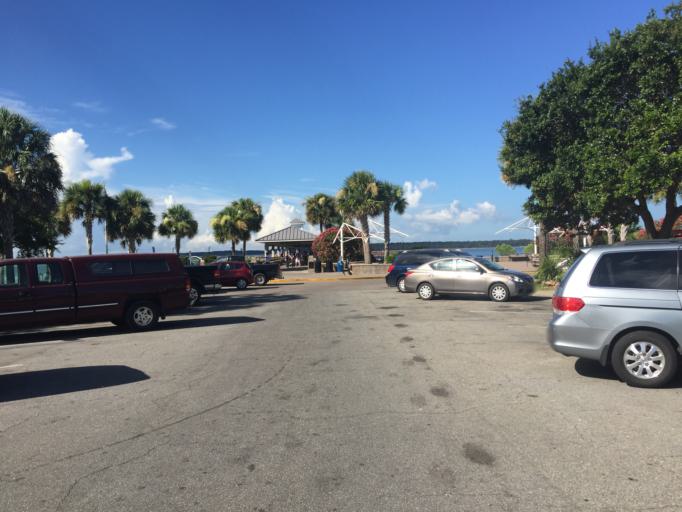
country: US
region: Georgia
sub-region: Glynn County
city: Saint Simons Island
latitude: 31.1346
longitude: -81.3964
